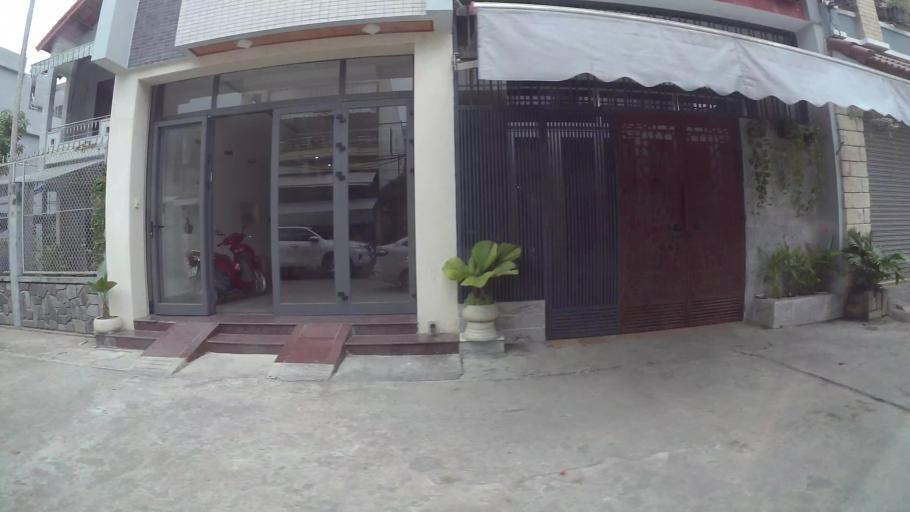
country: VN
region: Da Nang
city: Da Nang
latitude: 16.0798
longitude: 108.2138
